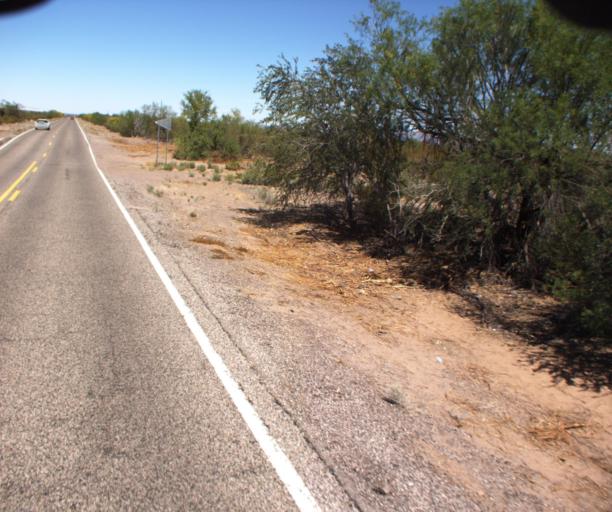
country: US
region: Arizona
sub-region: Pima County
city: Ajo
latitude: 32.2884
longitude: -112.7482
